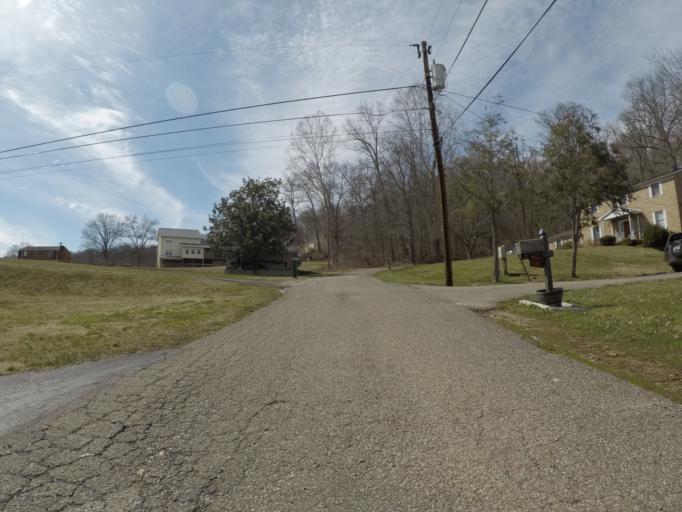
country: US
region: West Virginia
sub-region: Wayne County
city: Ceredo
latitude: 38.3609
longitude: -82.5364
